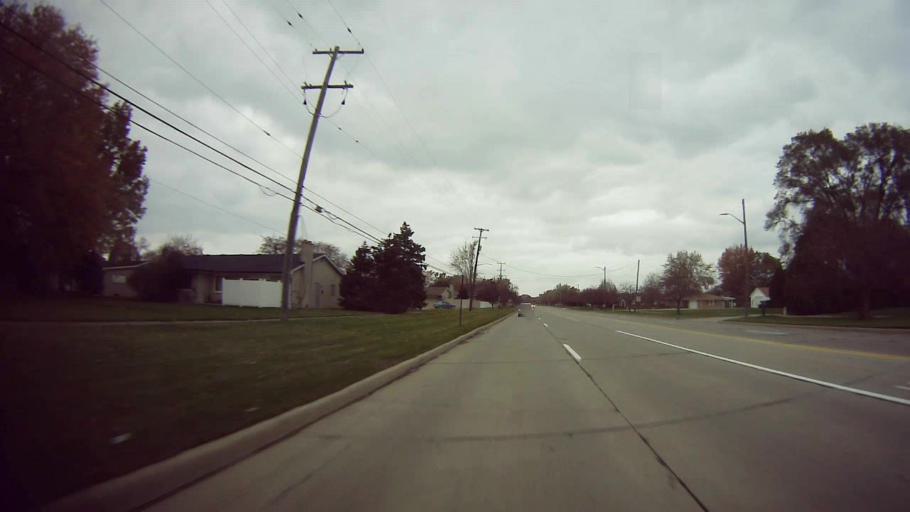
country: US
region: Michigan
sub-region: Macomb County
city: Center Line
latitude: 42.5287
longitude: -83.0079
